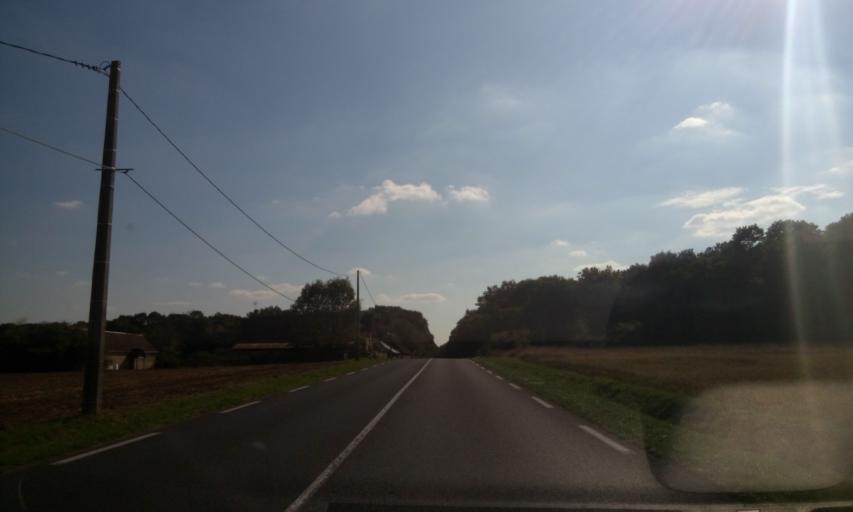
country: FR
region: Centre
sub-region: Departement d'Indre-et-Loire
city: Poce-sur-Cisse
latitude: 47.5122
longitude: 0.9972
